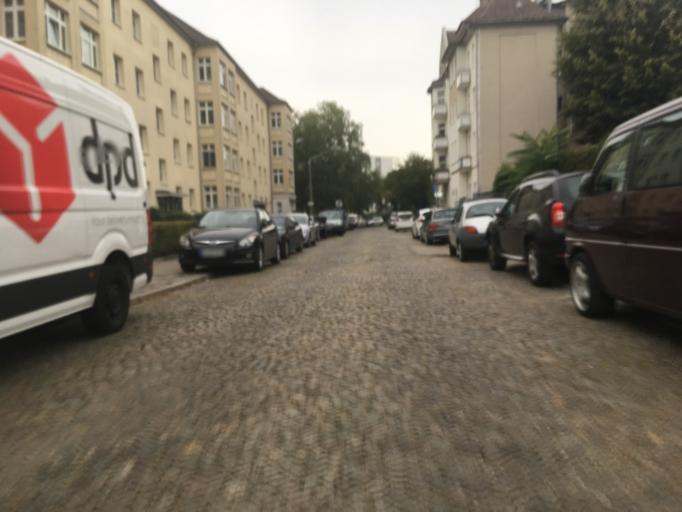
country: DE
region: Berlin
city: Fennpfuhl
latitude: 52.5374
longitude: 13.4798
